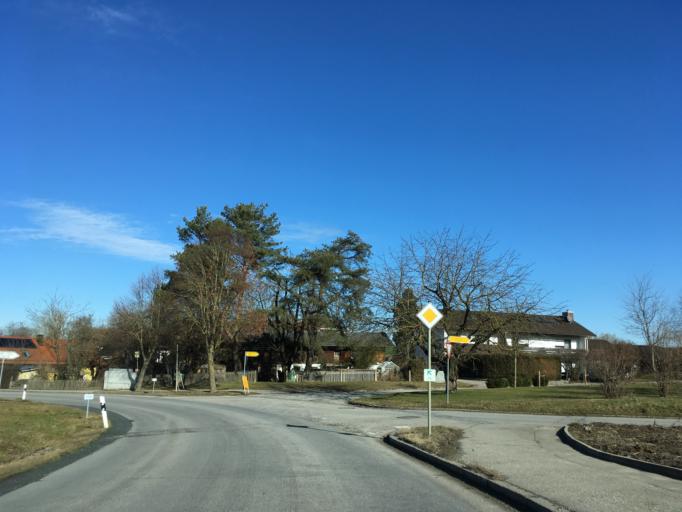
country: DE
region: Bavaria
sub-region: Upper Bavaria
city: Obertaufkirchen
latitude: 48.2578
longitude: 12.2851
